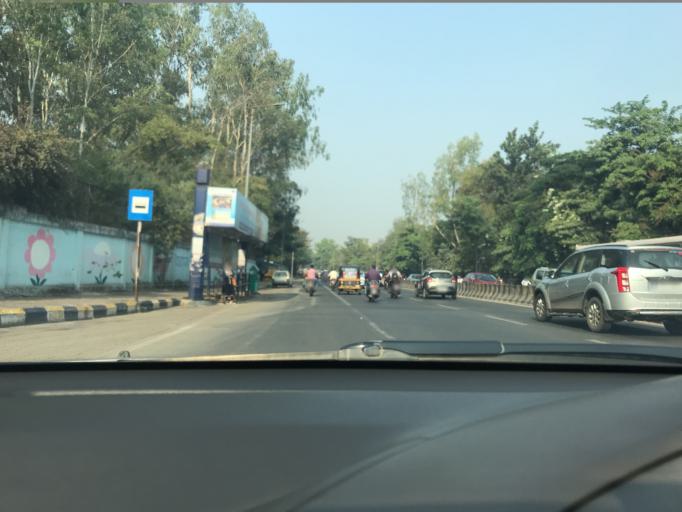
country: IN
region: Maharashtra
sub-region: Pune Division
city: Khadki
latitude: 18.5481
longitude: 73.8142
